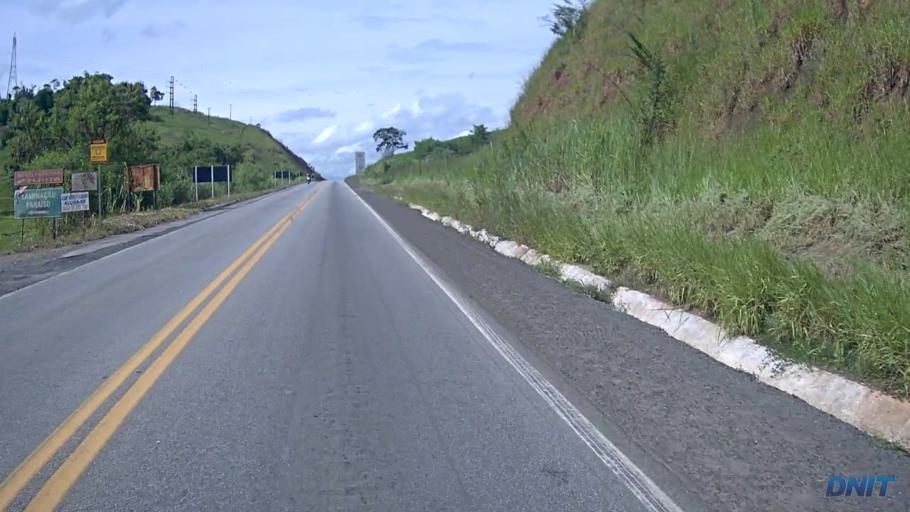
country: BR
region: Minas Gerais
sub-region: Ipatinga
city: Ipatinga
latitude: -19.4184
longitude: -42.4934
